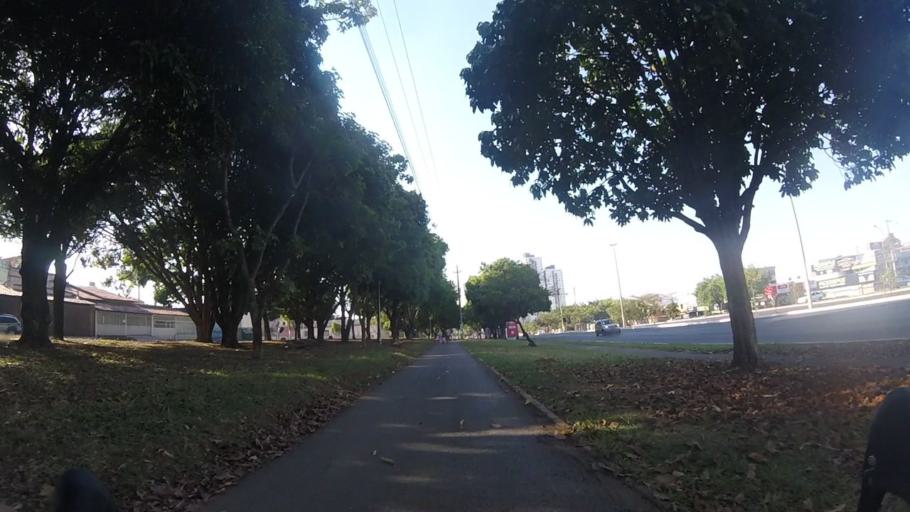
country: BR
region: Federal District
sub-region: Brasilia
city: Brasilia
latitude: -15.8353
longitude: -47.9862
